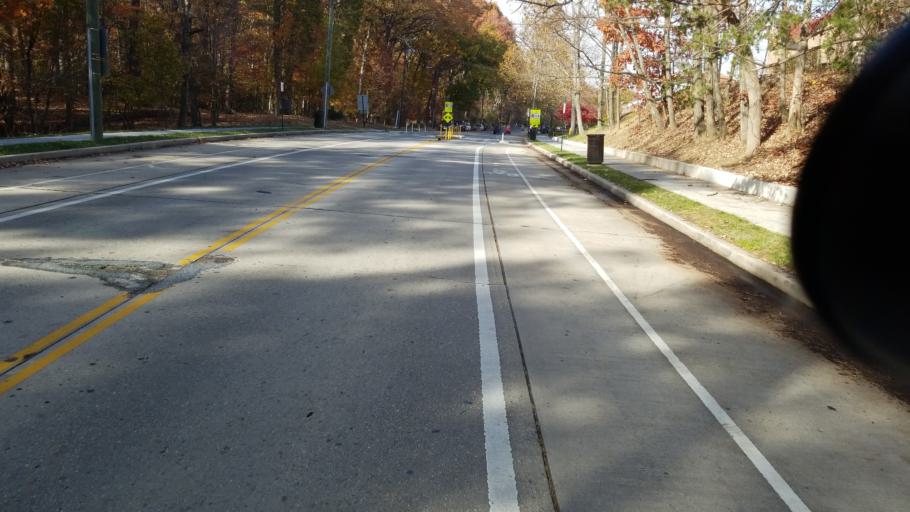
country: US
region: Maryland
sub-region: Prince George's County
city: Coral Hills
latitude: 38.8772
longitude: -76.9432
